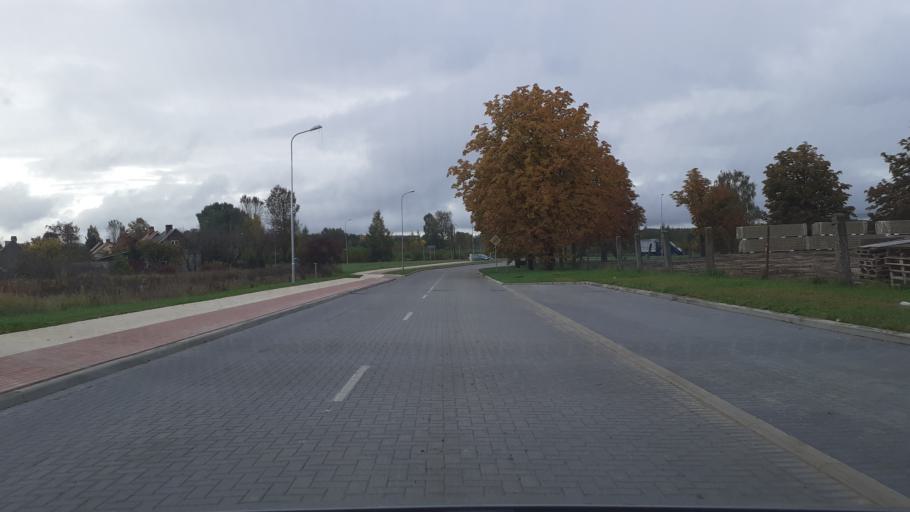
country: LV
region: Kuldigas Rajons
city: Kuldiga
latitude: 56.9809
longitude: 21.9492
